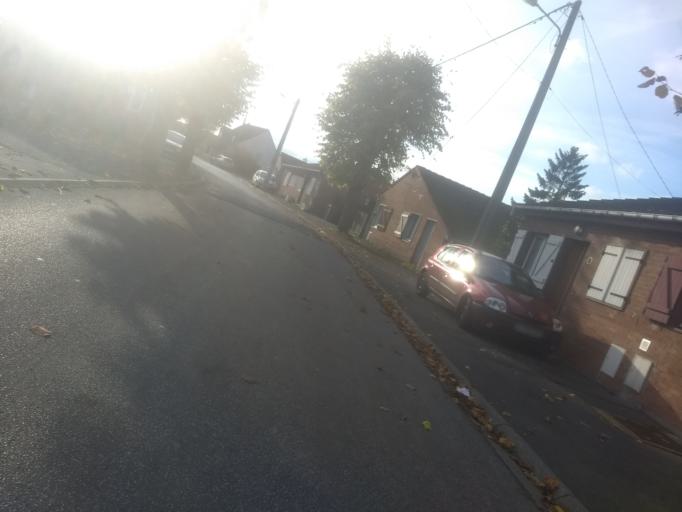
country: FR
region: Nord-Pas-de-Calais
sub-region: Departement du Pas-de-Calais
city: Arras
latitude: 50.2793
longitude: 2.7764
